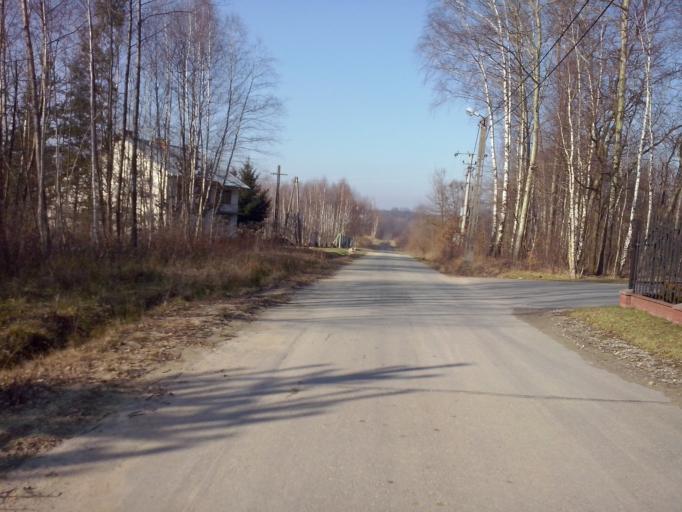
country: PL
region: Subcarpathian Voivodeship
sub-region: Powiat nizanski
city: Krzeszow
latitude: 50.4204
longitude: 22.3463
